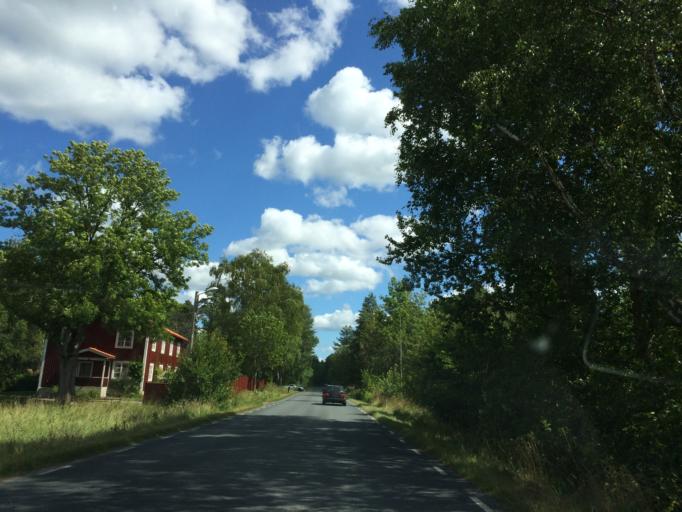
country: SE
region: Soedermanland
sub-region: Flens Kommun
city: Halleforsnas
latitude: 59.0662
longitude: 16.3645
